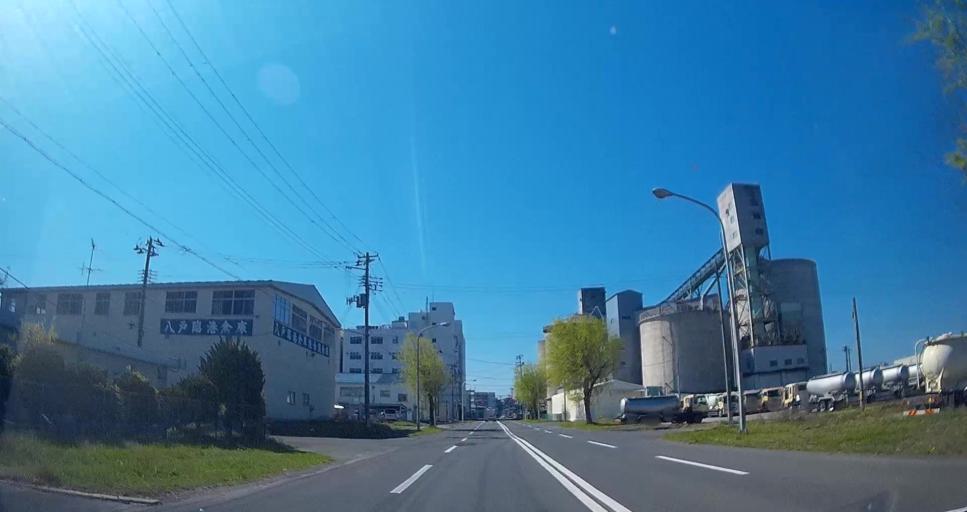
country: JP
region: Aomori
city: Hachinohe
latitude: 40.5286
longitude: 141.5445
